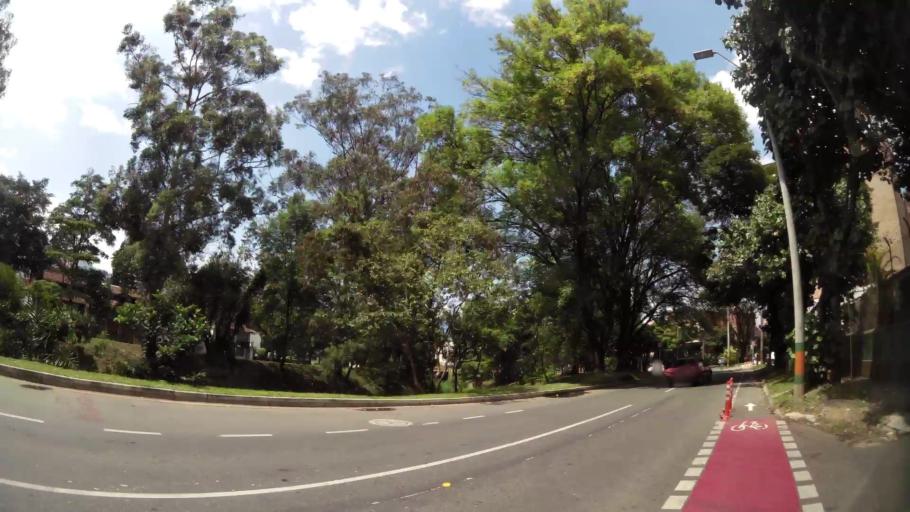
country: CO
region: Antioquia
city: Envigado
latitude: 6.1845
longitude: -75.5827
